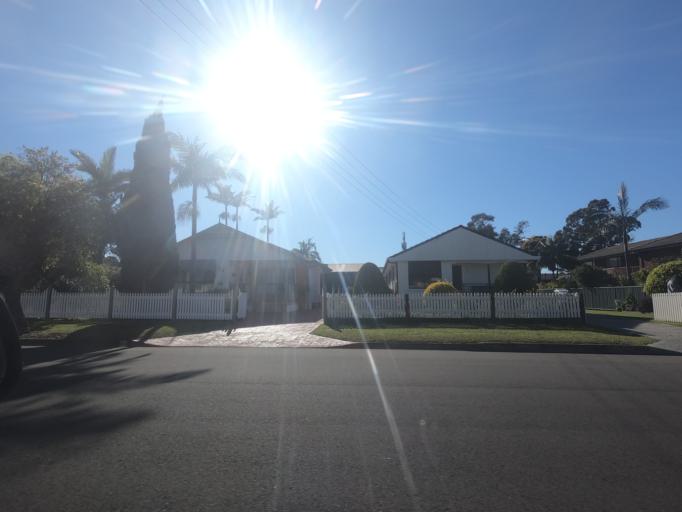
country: AU
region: New South Wales
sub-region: Wollongong
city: Fairy Meadow
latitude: -34.3872
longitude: 150.8895
